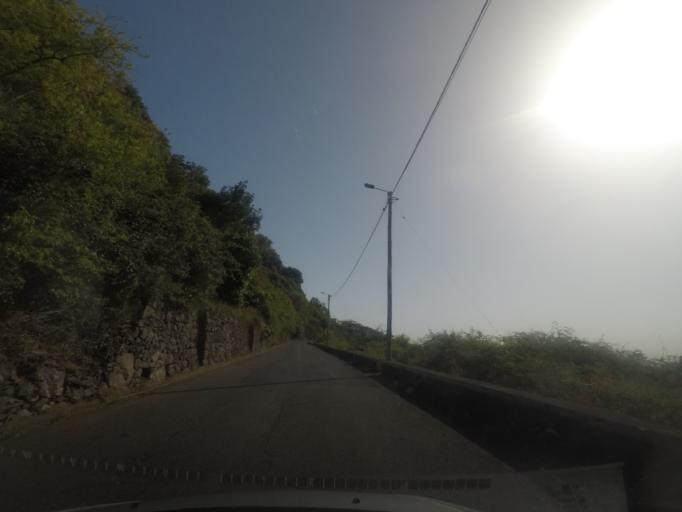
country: PT
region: Madeira
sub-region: Calheta
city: Arco da Calheta
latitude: 32.7296
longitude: -17.1641
